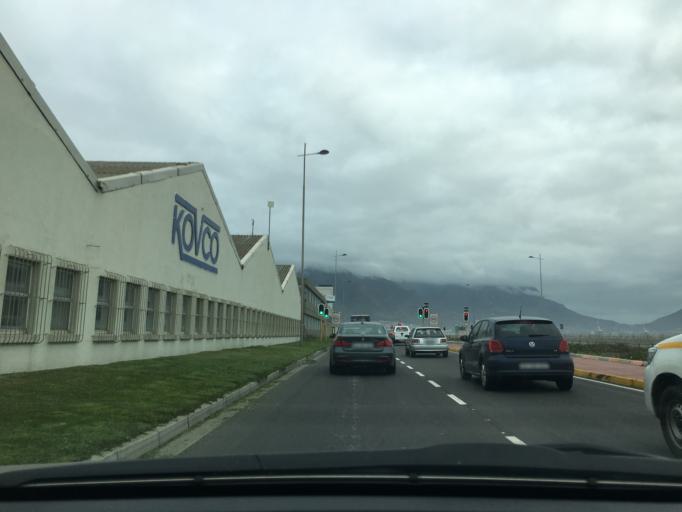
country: ZA
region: Western Cape
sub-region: City of Cape Town
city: Sunset Beach
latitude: -33.8986
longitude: 18.4799
